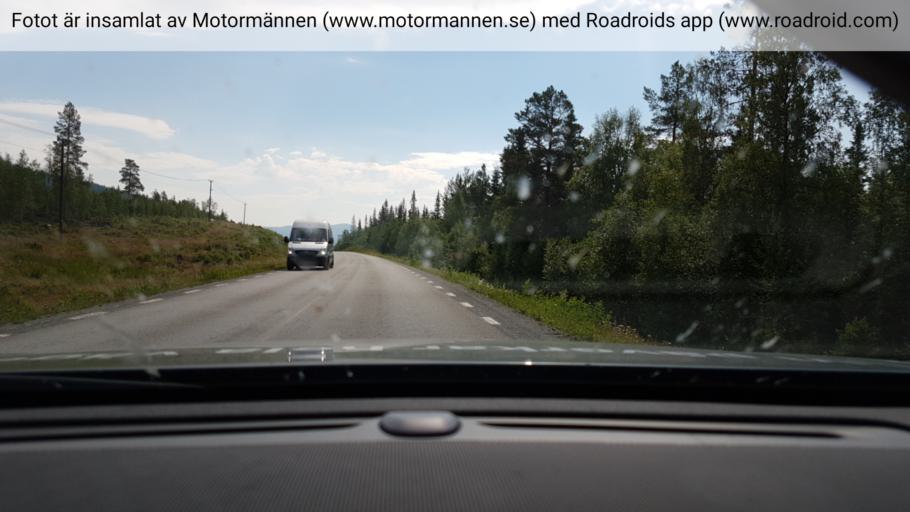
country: SE
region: Vaesterbotten
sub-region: Vilhelmina Kommun
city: Sjoberg
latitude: 65.5271
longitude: 15.6219
